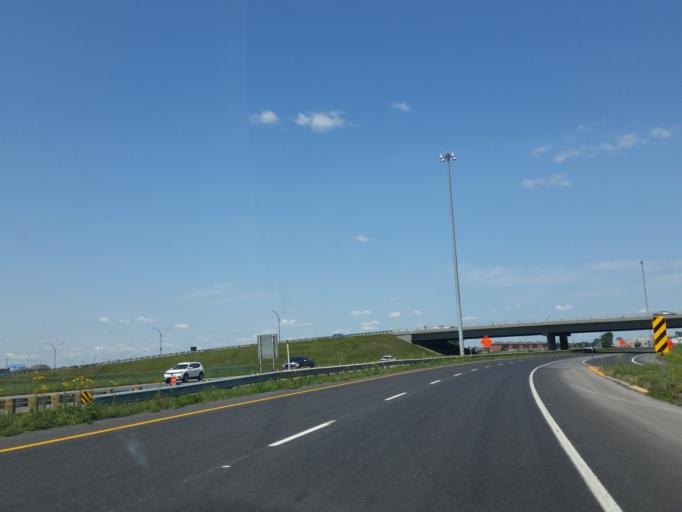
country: CA
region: Quebec
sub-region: Monteregie
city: Saint-Jean-sur-Richelieu
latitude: 45.3295
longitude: -73.2864
